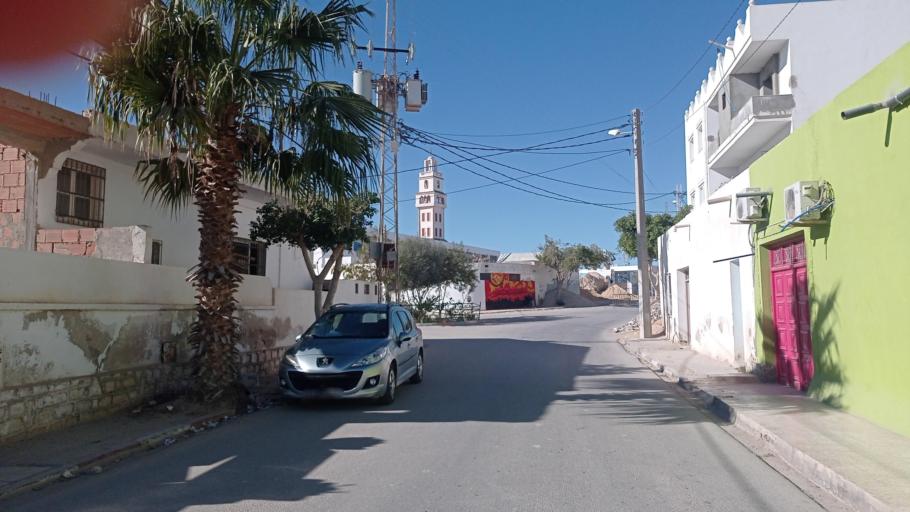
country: TN
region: Qabis
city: Gabes
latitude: 33.8480
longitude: 10.1090
